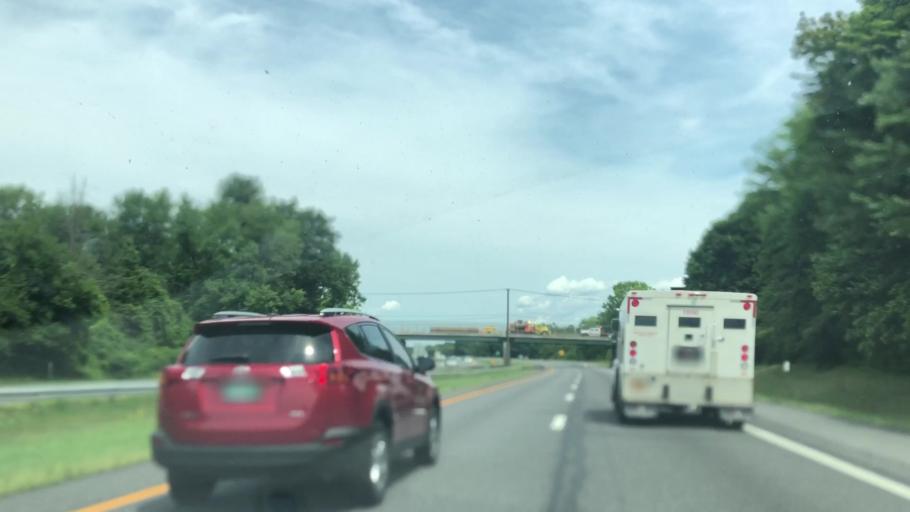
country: US
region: New York
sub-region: Rensselaer County
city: Castleton-on-Hudson
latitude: 42.5286
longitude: -73.7864
